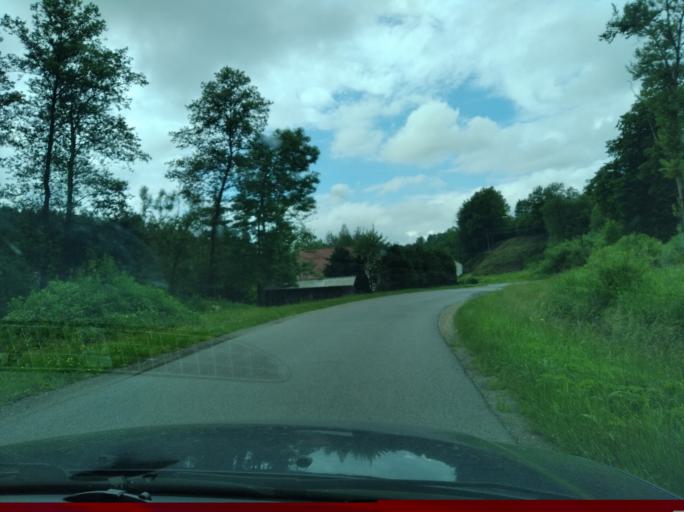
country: PL
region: Subcarpathian Voivodeship
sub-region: Powiat przemyski
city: Dubiecko
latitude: 49.8382
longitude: 22.3991
